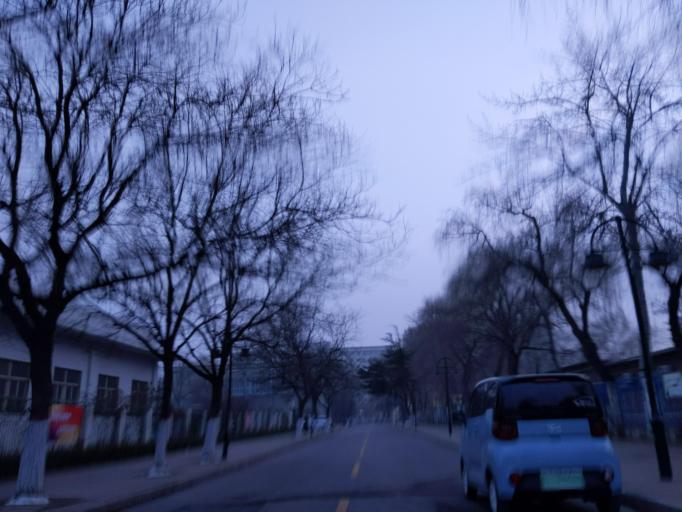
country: CN
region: Henan Sheng
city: Zhongyuanlu
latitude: 35.7798
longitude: 115.0741
